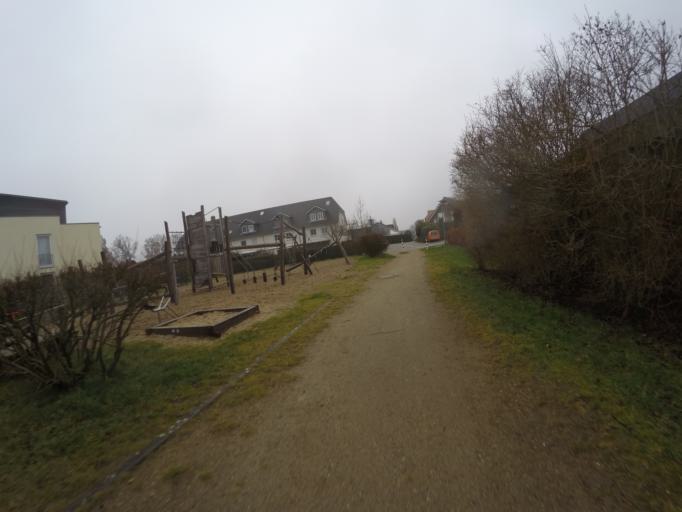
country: DE
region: Schleswig-Holstein
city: Quickborn
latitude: 53.7326
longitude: 9.8879
